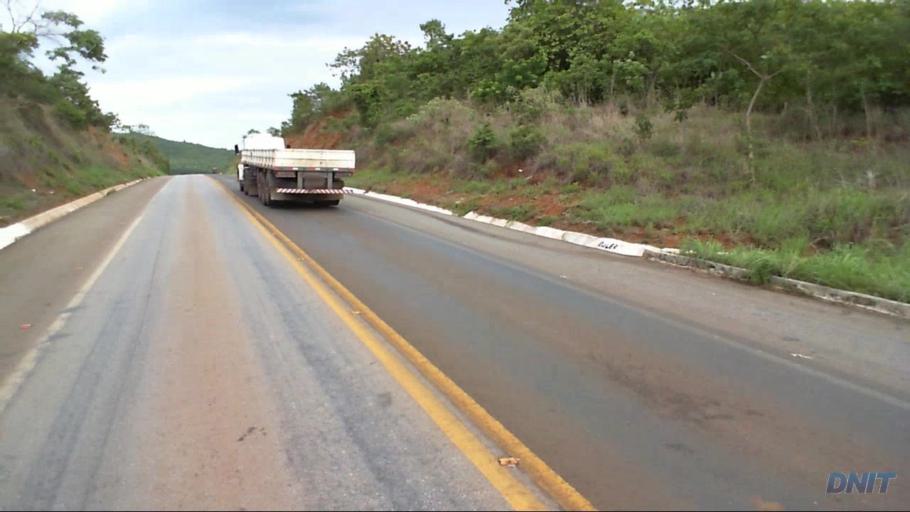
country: BR
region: Goias
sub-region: Barro Alto
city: Barro Alto
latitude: -14.9381
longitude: -48.9425
